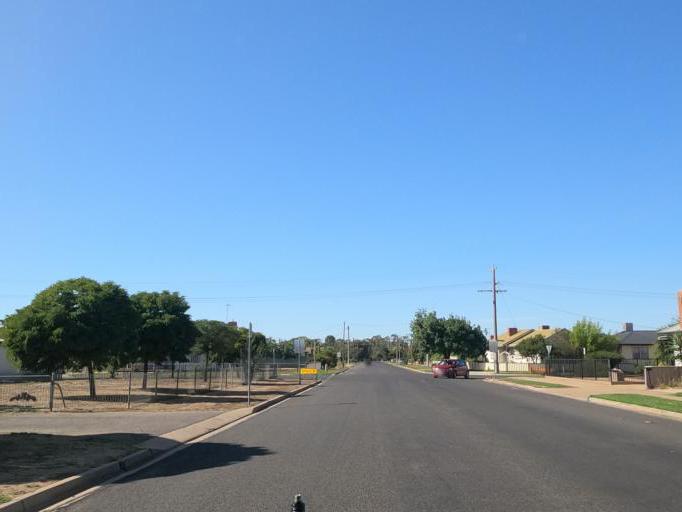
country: AU
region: Victoria
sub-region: Moira
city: Yarrawonga
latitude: -36.0215
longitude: 146.0054
